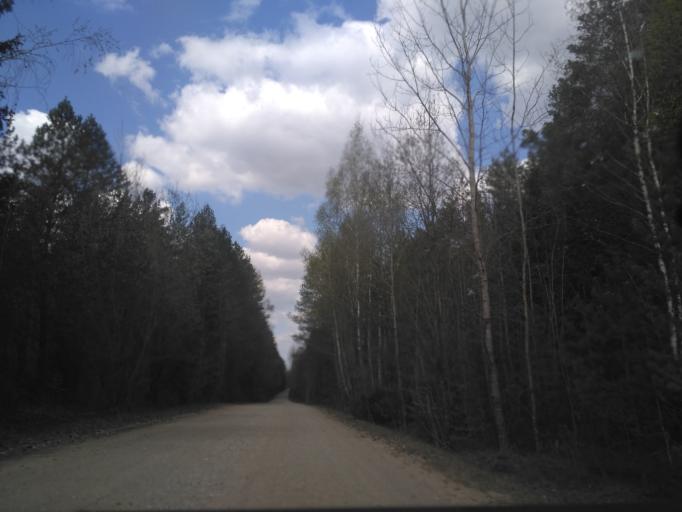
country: BY
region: Minsk
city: Il'ya
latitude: 54.2977
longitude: 27.2774
